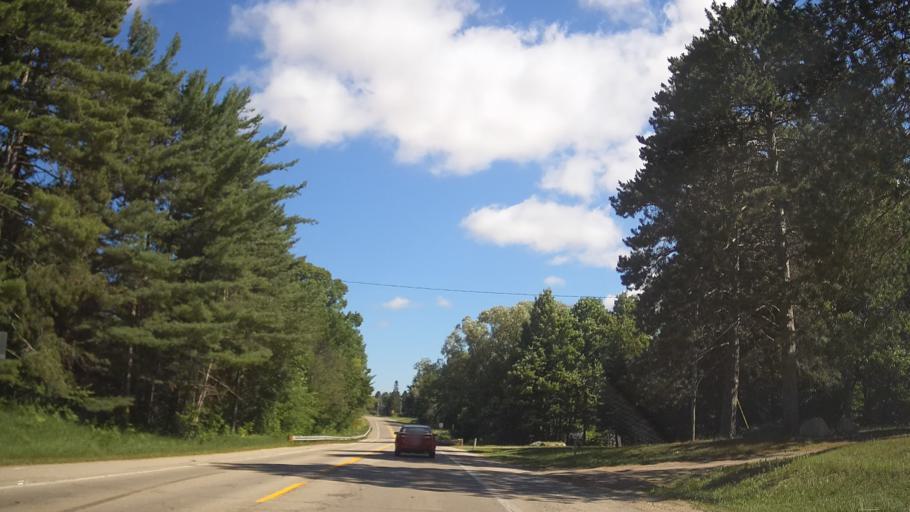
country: US
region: Michigan
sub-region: Cheboygan County
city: Indian River
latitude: 45.4673
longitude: -84.7814
